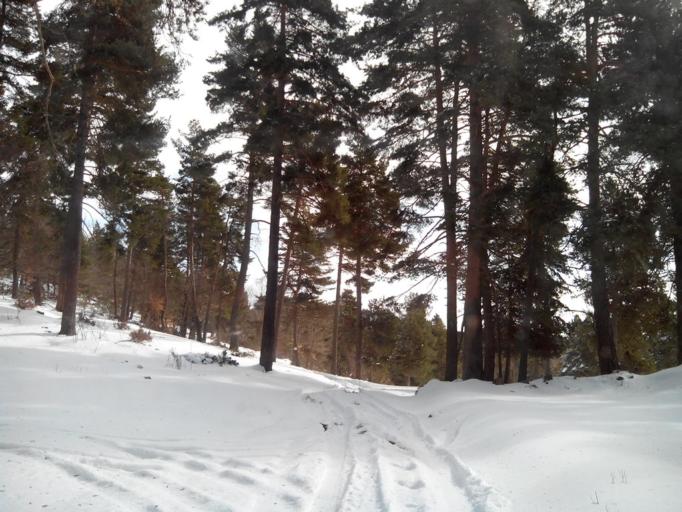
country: ES
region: Catalonia
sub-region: Provincia de Barcelona
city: Sant Julia de Cerdanyola
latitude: 42.2029
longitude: 1.9348
